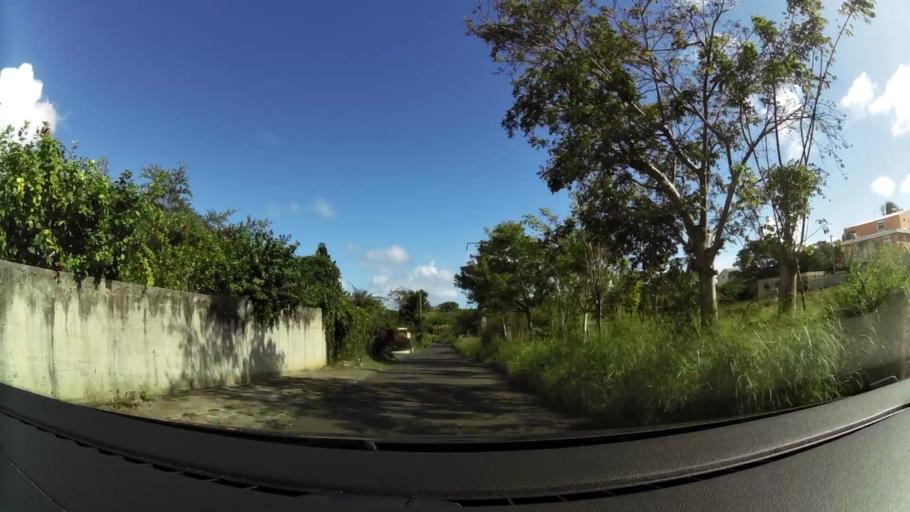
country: GP
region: Guadeloupe
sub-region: Guadeloupe
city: Sainte-Anne
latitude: 16.2351
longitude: -61.3796
